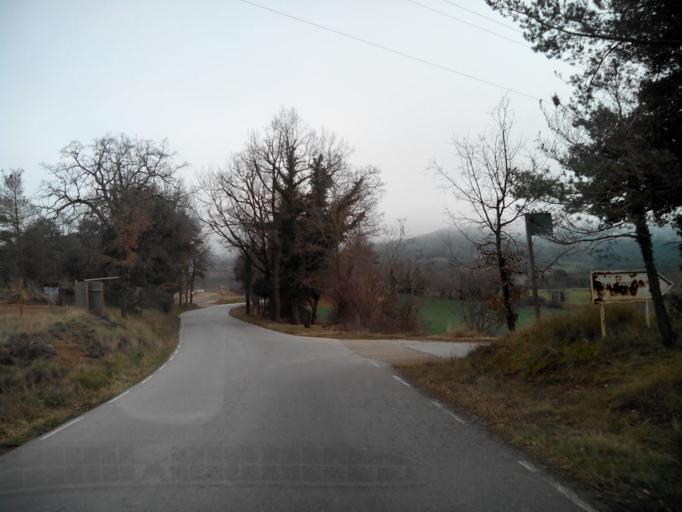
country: ES
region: Catalonia
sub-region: Provincia de Barcelona
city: Olost
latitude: 41.9782
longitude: 2.1503
